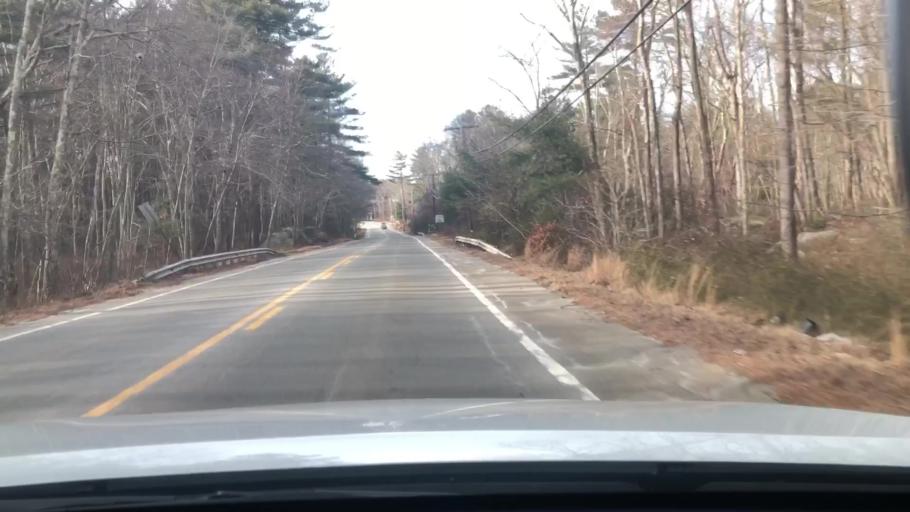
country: US
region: Massachusetts
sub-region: Worcester County
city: Hopedale
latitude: 42.1542
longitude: -71.5657
